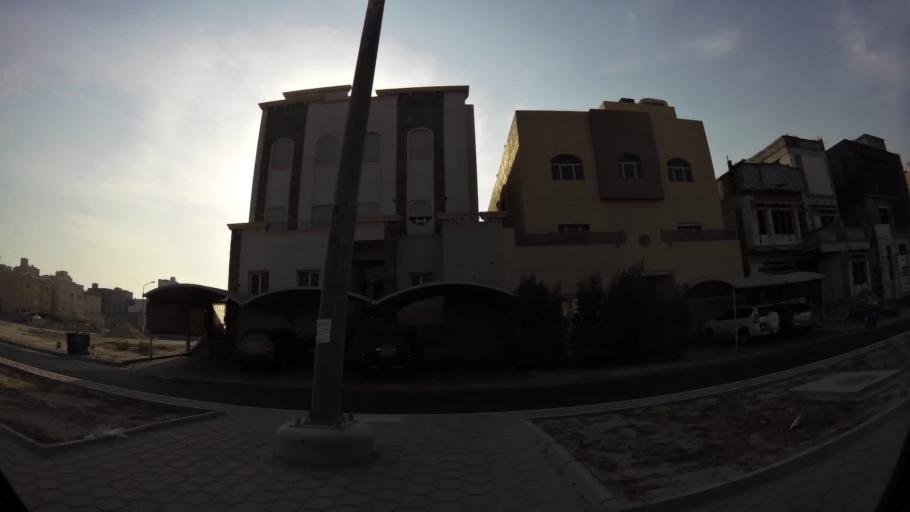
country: KW
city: Al Funaytis
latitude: 29.2344
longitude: 48.0883
